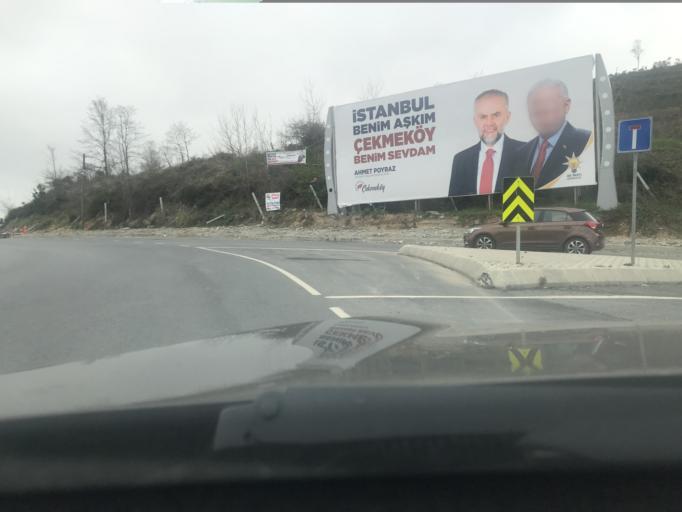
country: TR
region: Istanbul
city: Umraniye
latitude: 41.0561
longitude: 29.1685
